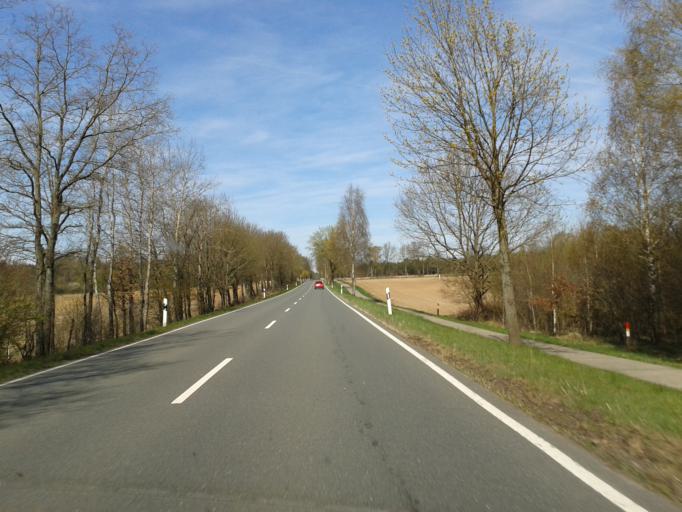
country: DE
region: Lower Saxony
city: Eimke
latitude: 52.9710
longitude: 10.2756
